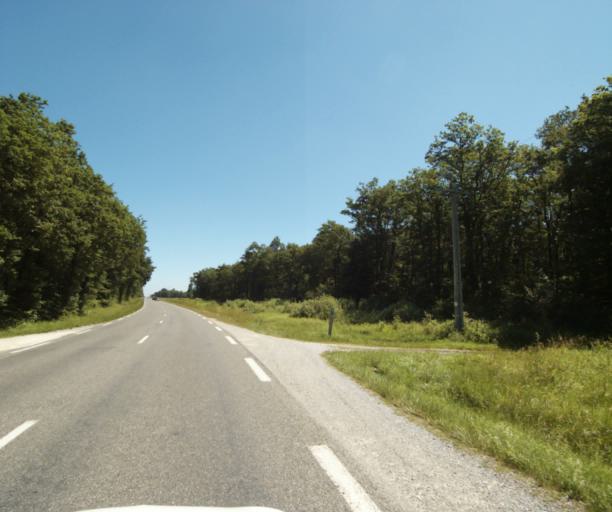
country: FR
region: Rhone-Alpes
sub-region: Departement de la Haute-Savoie
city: Veigy-Foncenex
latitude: 46.2866
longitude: 6.2658
